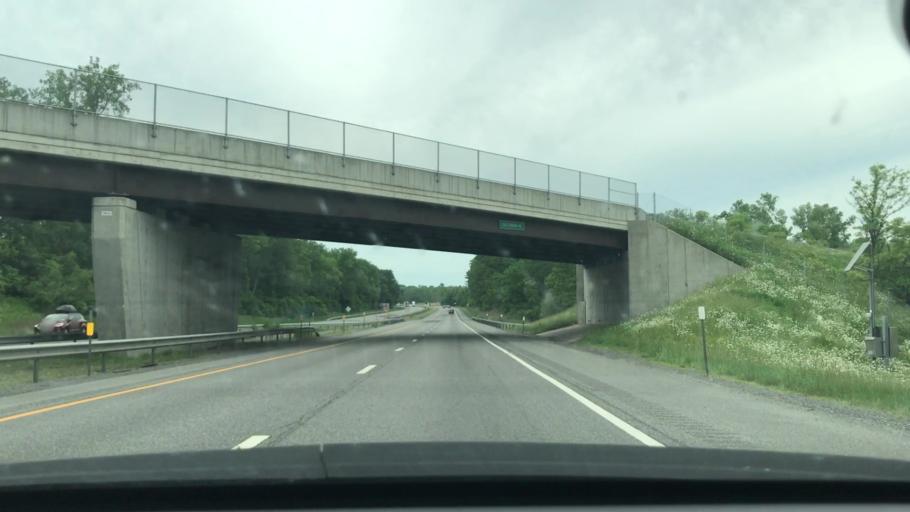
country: US
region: New York
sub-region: Onondaga County
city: Liverpool
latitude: 43.1181
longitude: -76.2257
